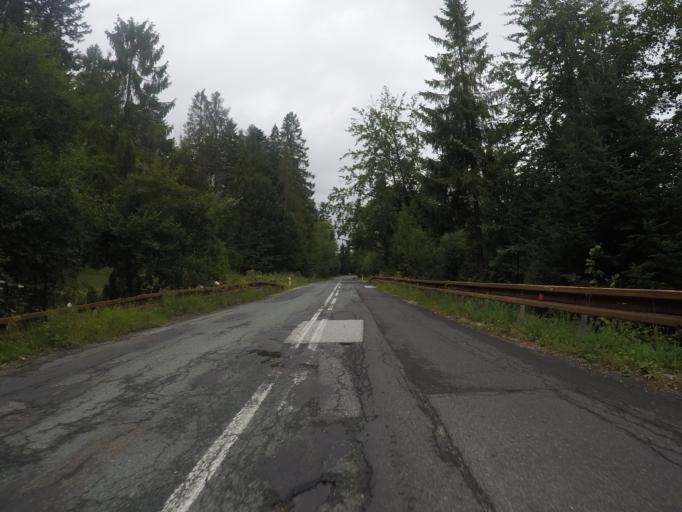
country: SK
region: Kosicky
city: Spisska Nova Ves
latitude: 48.8795
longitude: 20.5325
